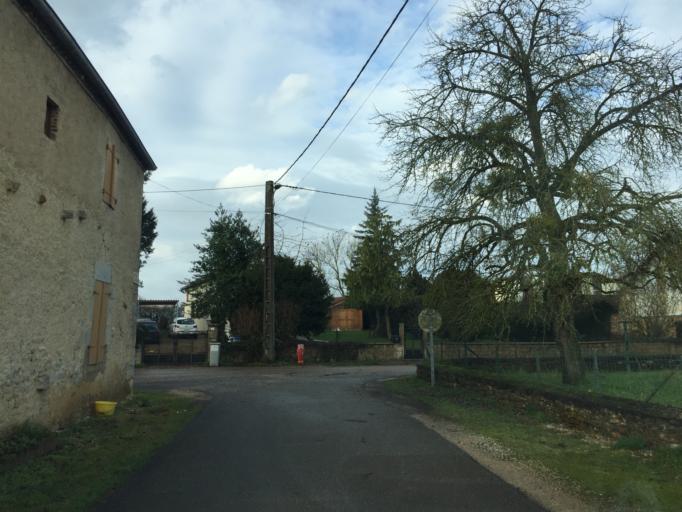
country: FR
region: Franche-Comte
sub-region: Departement du Jura
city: Mont-sous-Vaudrey
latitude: 46.9793
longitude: 5.6201
